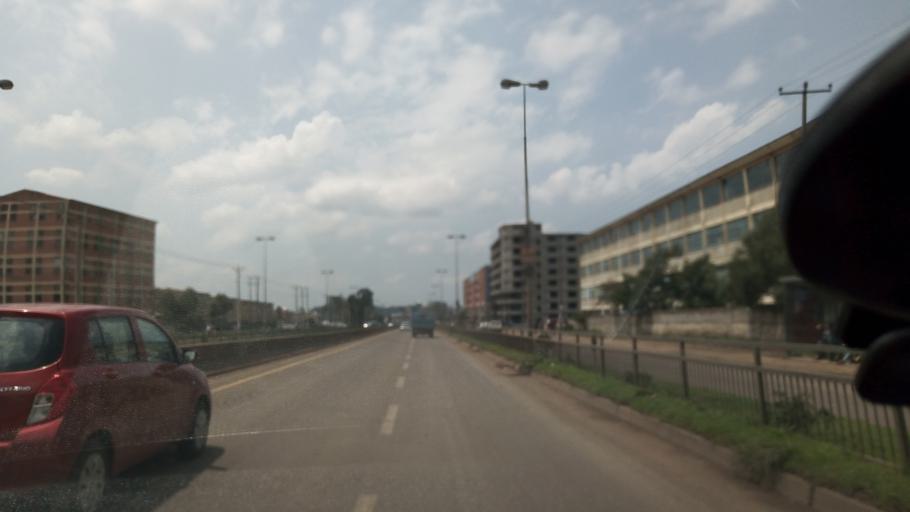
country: ET
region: Adis Abeba
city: Addis Ababa
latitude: 8.9681
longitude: 38.7232
